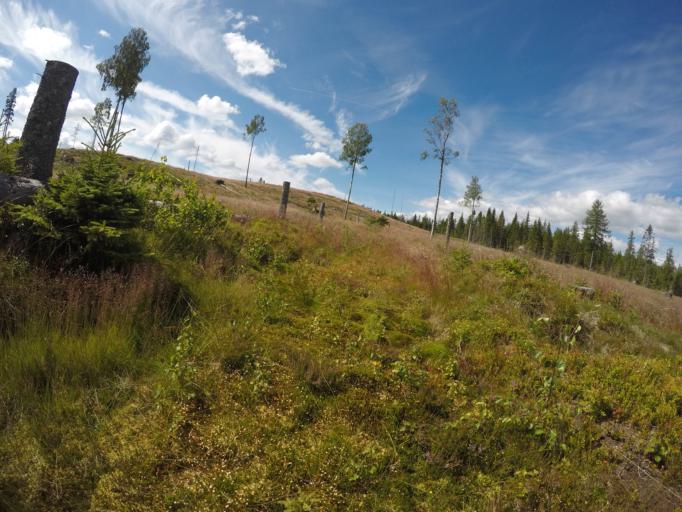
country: SE
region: Vaermland
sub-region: Filipstads Kommun
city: Lesjofors
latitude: 60.0926
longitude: 14.4621
